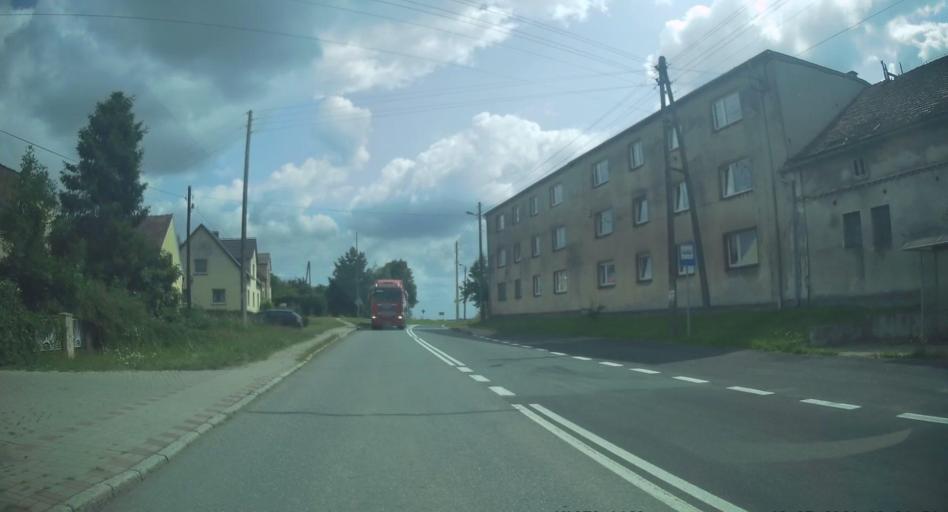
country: PL
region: Opole Voivodeship
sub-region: Powiat prudnicki
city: Twardawa
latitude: 50.3405
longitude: 17.9454
